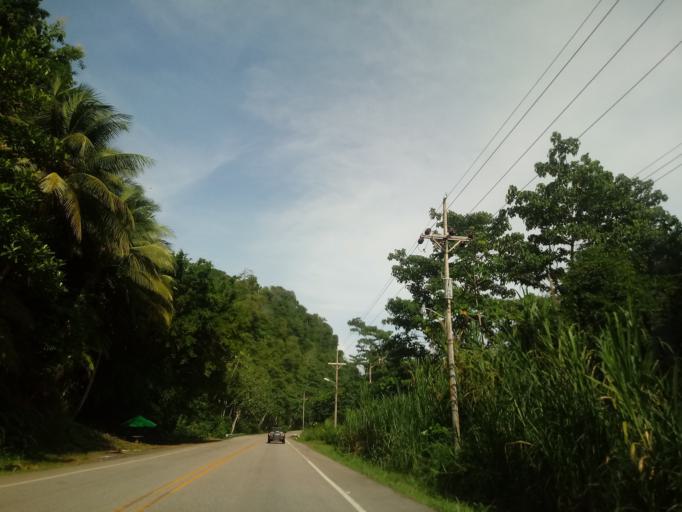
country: CR
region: San Jose
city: Daniel Flores
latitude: 9.2042
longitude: -83.7943
